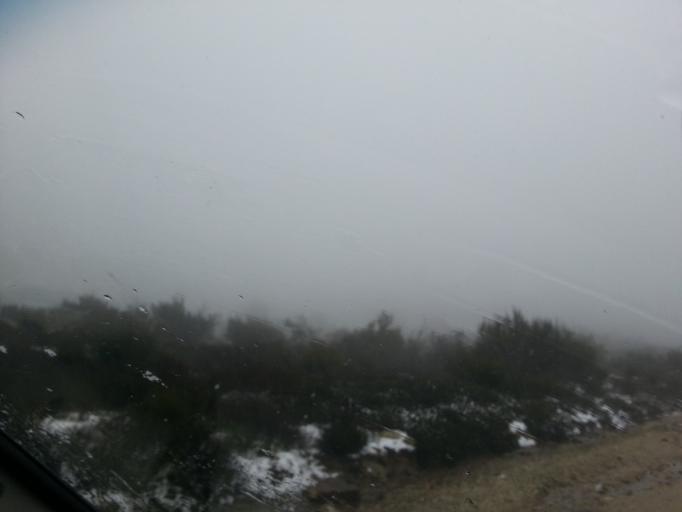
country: PT
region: Guarda
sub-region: Celorico da Beira
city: Celorico da Beira
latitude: 40.5305
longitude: -7.4459
